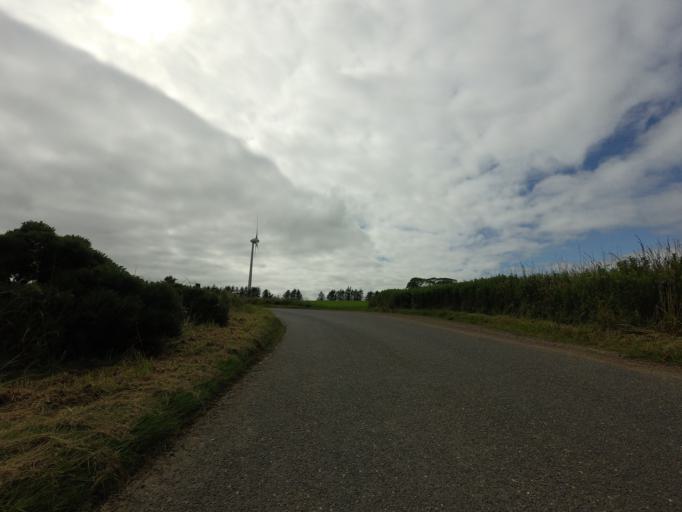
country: GB
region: Scotland
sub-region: Aberdeenshire
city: Turriff
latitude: 57.5456
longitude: -2.2910
